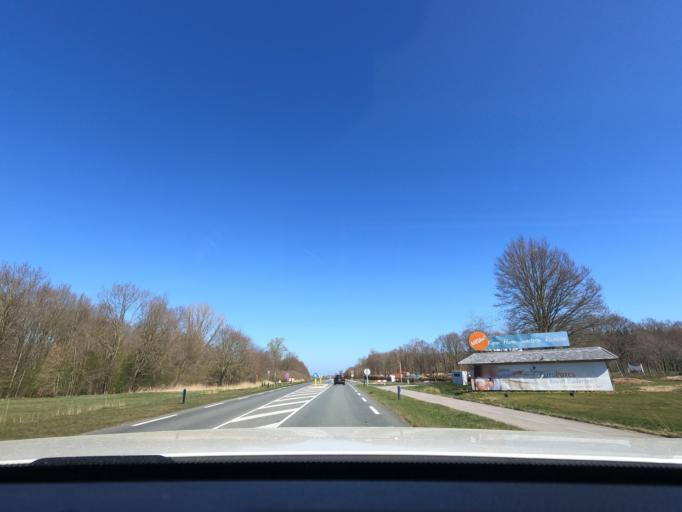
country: NL
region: Gelderland
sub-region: Gemeente Elburg
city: Elburg
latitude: 52.4469
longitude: 5.7912
